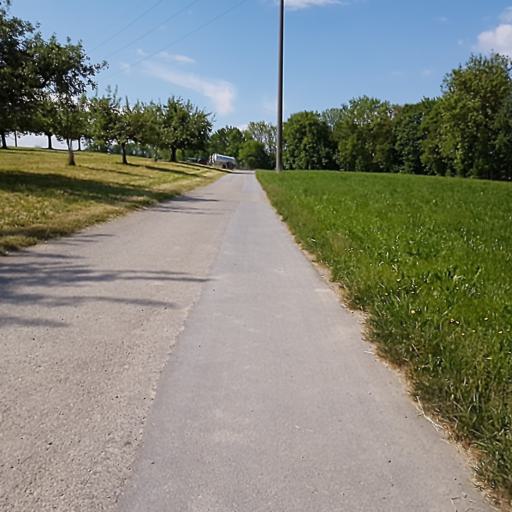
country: CH
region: Thurgau
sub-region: Arbon District
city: Amriswil
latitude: 47.5581
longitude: 9.3006
